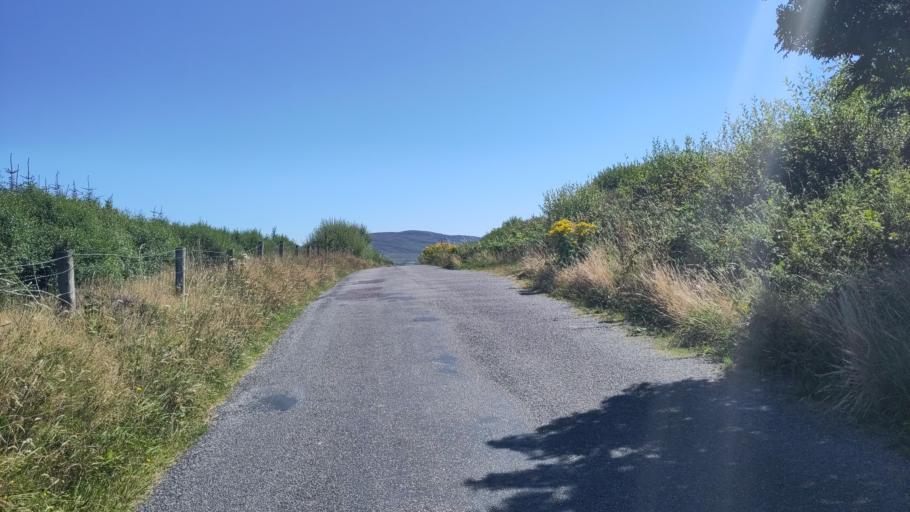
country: IE
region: Munster
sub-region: Ciarrai
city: Kenmare
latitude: 51.6671
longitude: -9.9116
